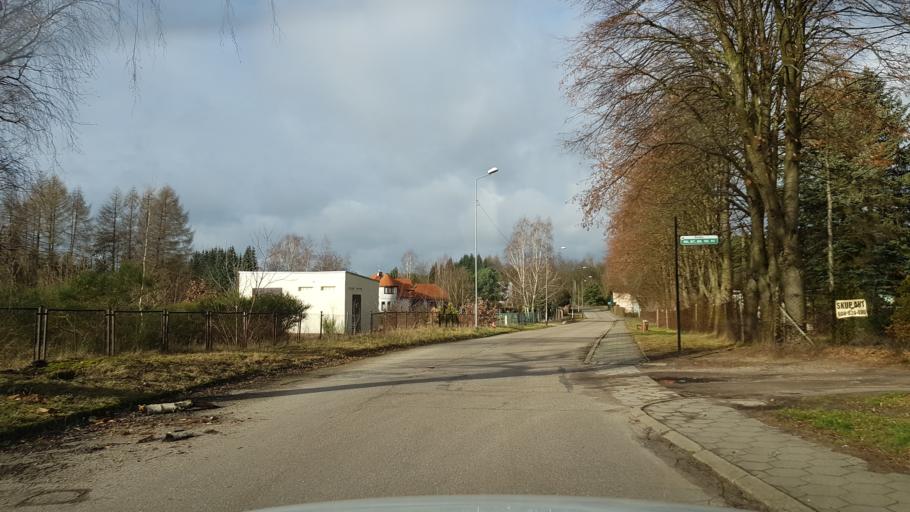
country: PL
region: West Pomeranian Voivodeship
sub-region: Powiat swidwinski
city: Rabino
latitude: 53.7756
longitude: 15.9638
